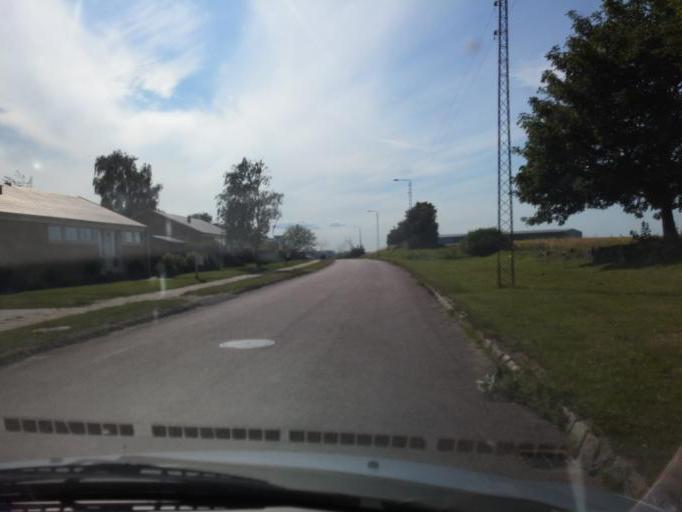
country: DK
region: South Denmark
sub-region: Kerteminde Kommune
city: Munkebo
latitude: 55.4653
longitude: 10.5590
